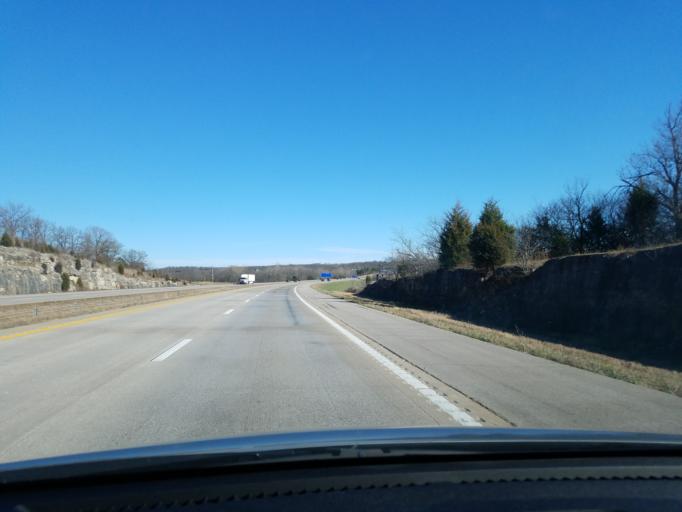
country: US
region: Missouri
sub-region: Pulaski County
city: Richland
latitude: 37.7605
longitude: -92.5269
